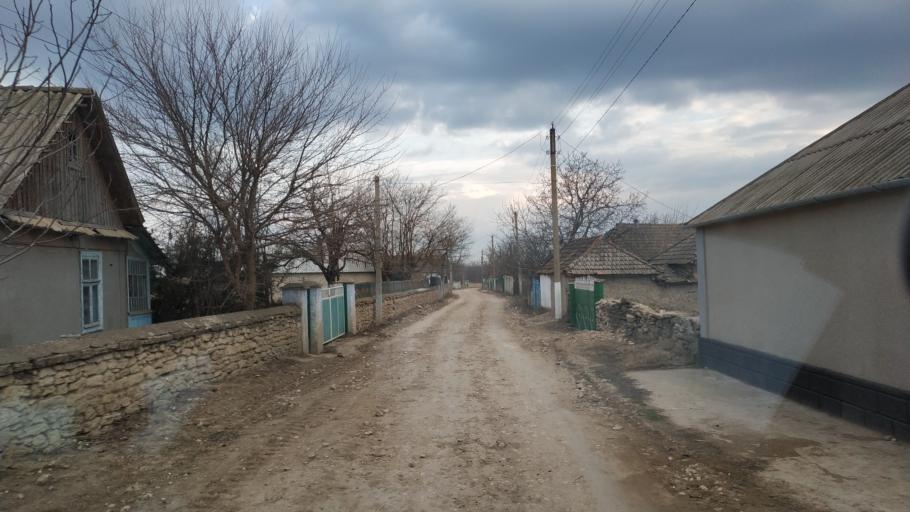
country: MD
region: Telenesti
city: Grigoriopol
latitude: 47.0238
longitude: 29.3505
